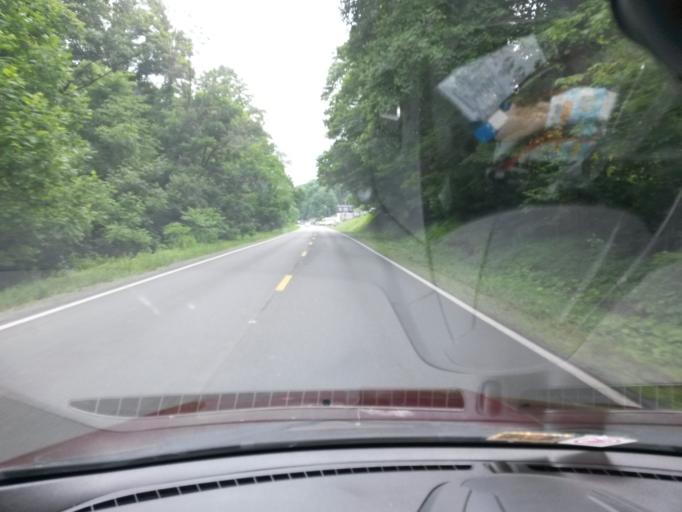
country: US
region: West Virginia
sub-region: Mercer County
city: Bluefield
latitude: 37.2797
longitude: -81.1847
